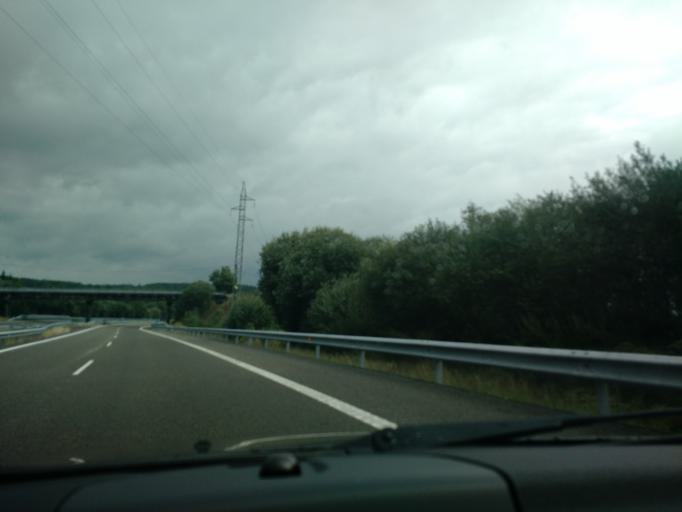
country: ES
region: Galicia
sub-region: Provincia da Coruna
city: Oroso
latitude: 42.9652
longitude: -8.4546
